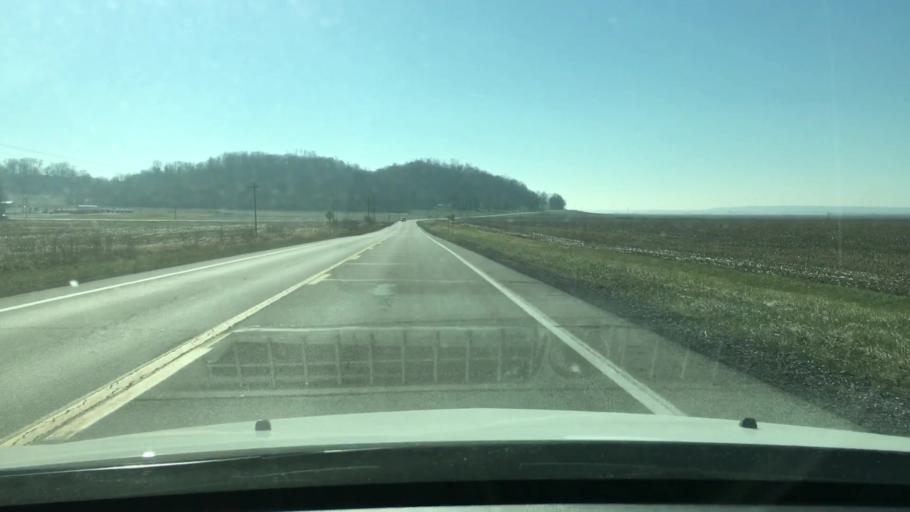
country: US
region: Illinois
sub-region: Morgan County
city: Meredosia
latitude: 39.7090
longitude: -90.5686
